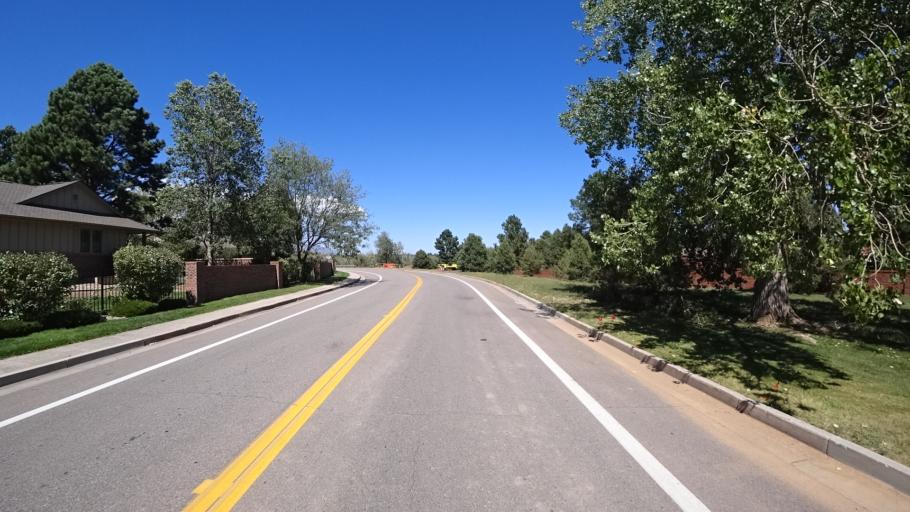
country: US
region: Colorado
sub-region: El Paso County
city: Colorado Springs
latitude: 38.7926
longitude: -104.8276
